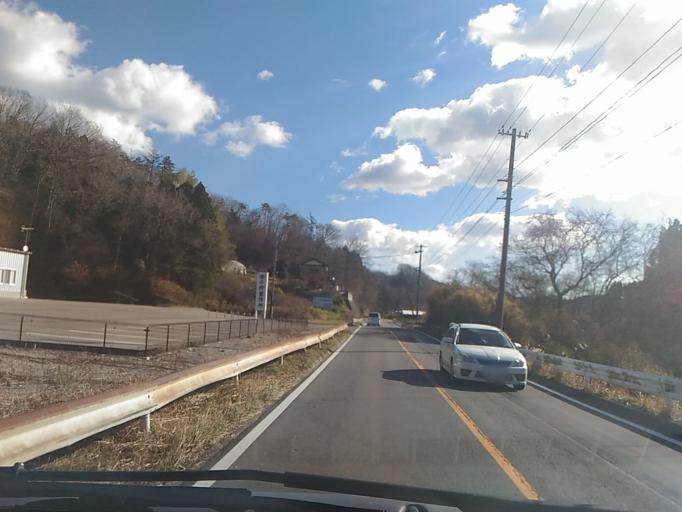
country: JP
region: Fukushima
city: Iwaki
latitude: 37.0089
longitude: 140.7791
